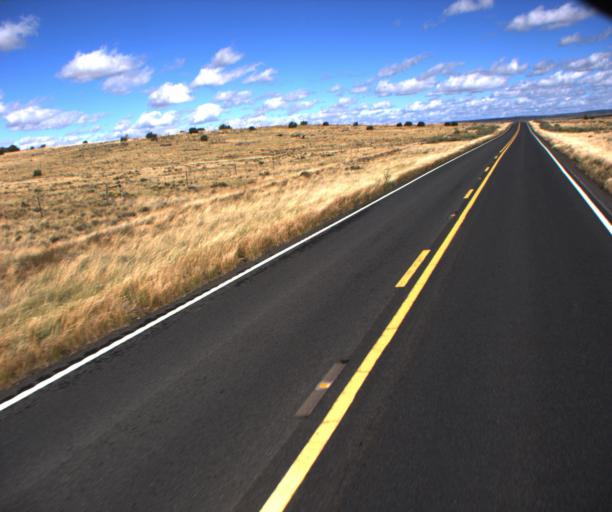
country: US
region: Arizona
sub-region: Apache County
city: Houck
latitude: 34.9703
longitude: -109.2273
